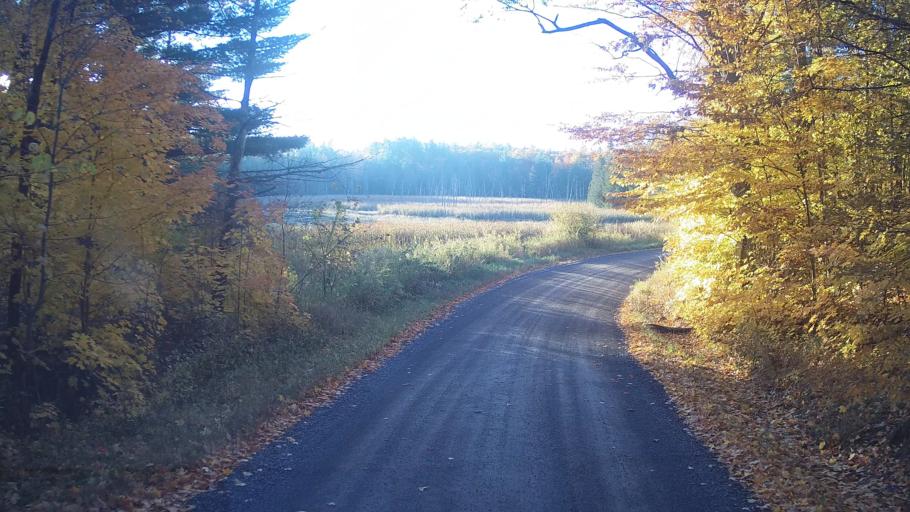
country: CA
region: Ontario
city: Arnprior
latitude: 45.3383
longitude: -76.3527
